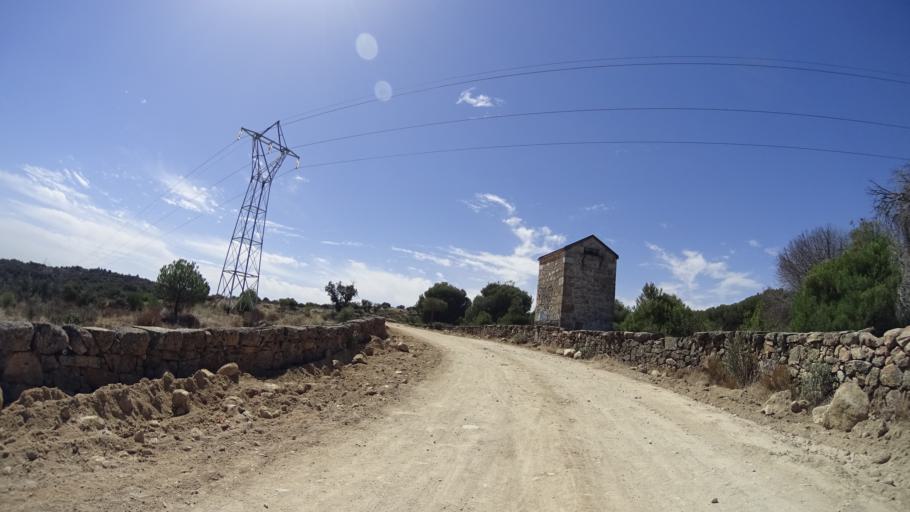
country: ES
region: Madrid
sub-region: Provincia de Madrid
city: Torrelodones
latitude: 40.5677
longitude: -3.9391
